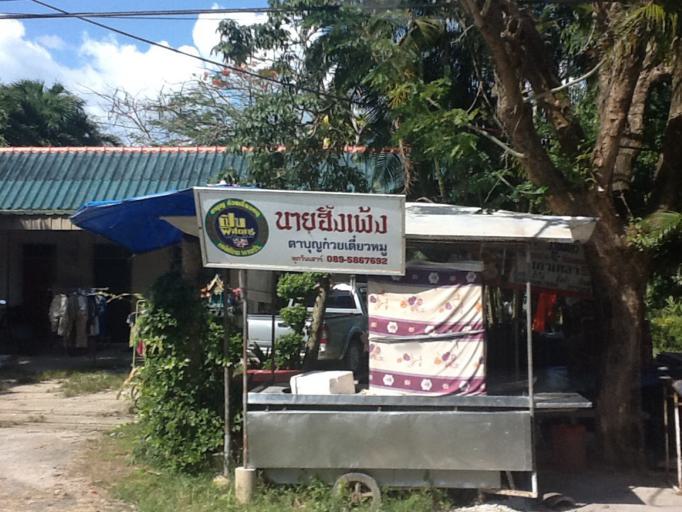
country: TH
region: Phuket
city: Thalang
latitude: 8.1247
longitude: 98.3162
